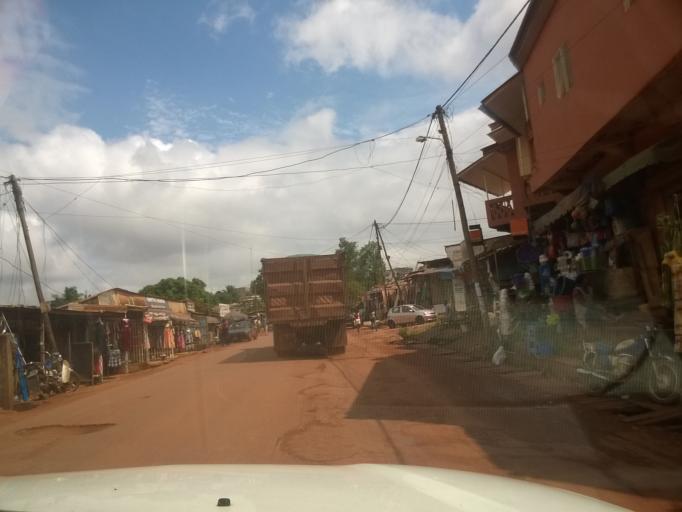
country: CM
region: Centre
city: Yaounde
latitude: 3.8714
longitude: 11.5418
